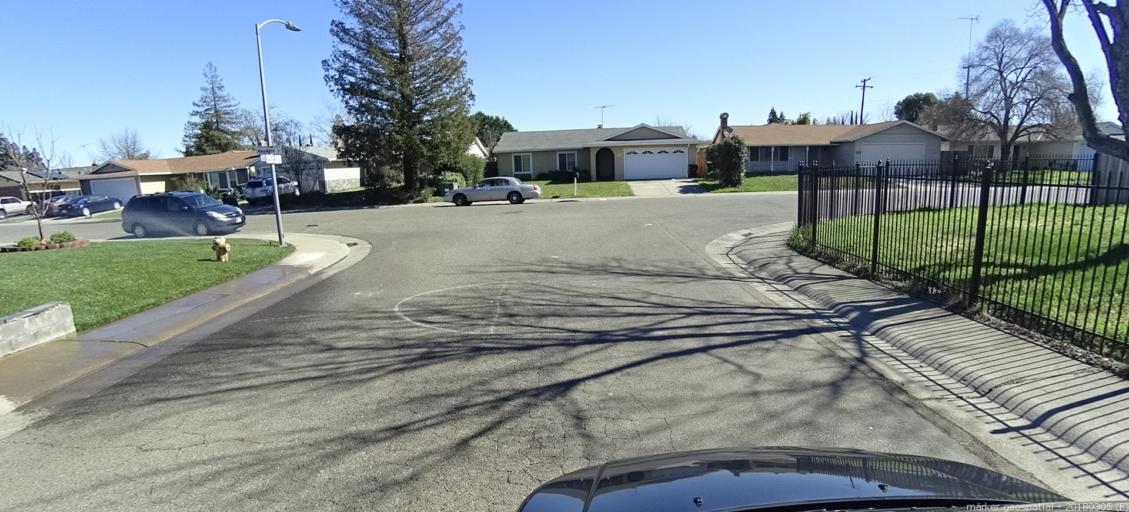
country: US
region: California
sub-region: Sacramento County
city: Florin
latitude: 38.4925
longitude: -121.3880
